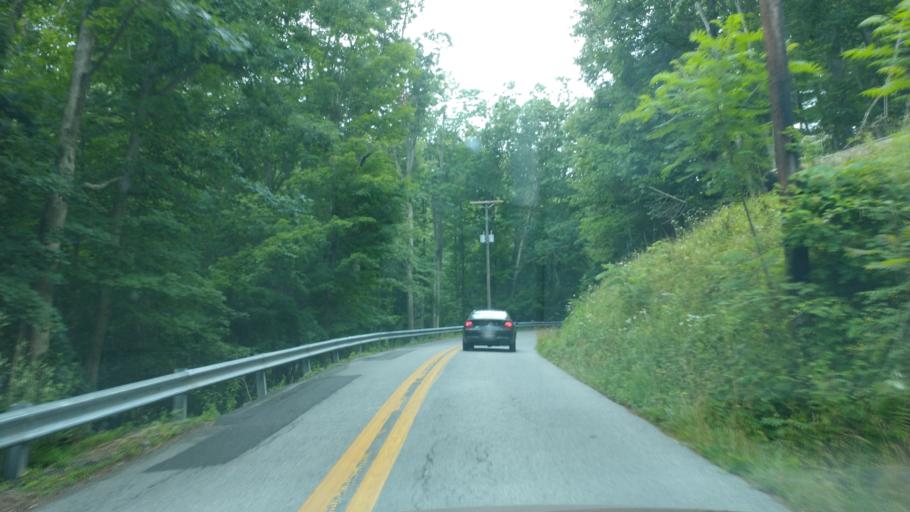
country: US
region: West Virginia
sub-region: Mercer County
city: Athens
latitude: 37.4229
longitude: -81.0042
